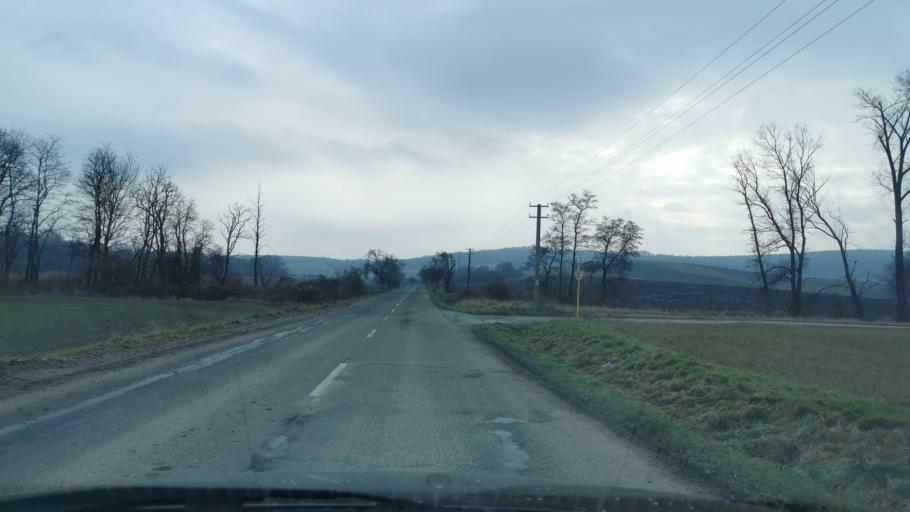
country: SK
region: Trnavsky
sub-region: Okres Skalica
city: Skalica
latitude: 48.7566
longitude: 17.2866
